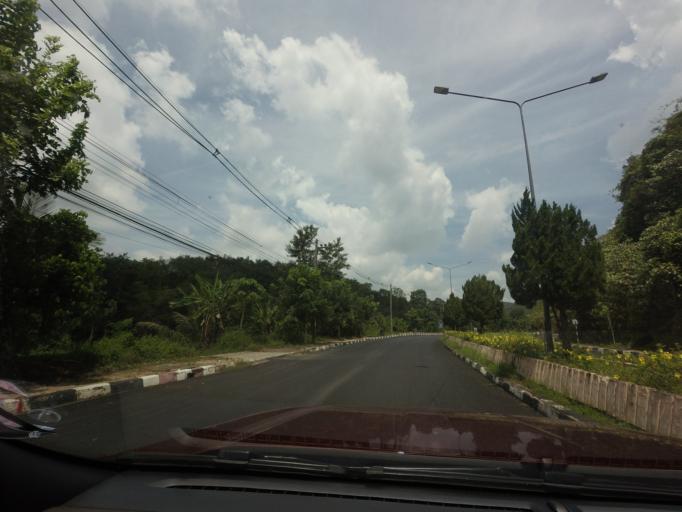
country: TH
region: Yala
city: Betong
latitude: 5.7646
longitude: 101.0504
